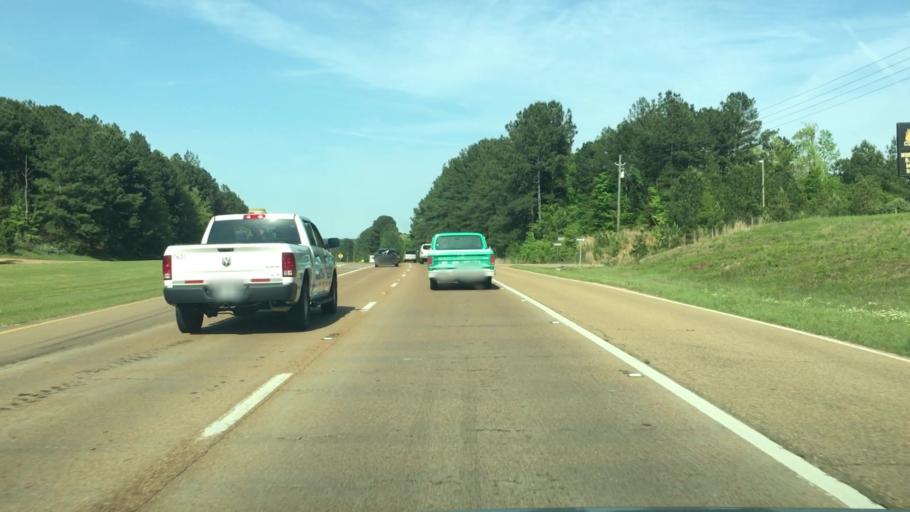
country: US
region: Mississippi
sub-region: Rankin County
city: Brandon
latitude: 32.3628
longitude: -89.9923
